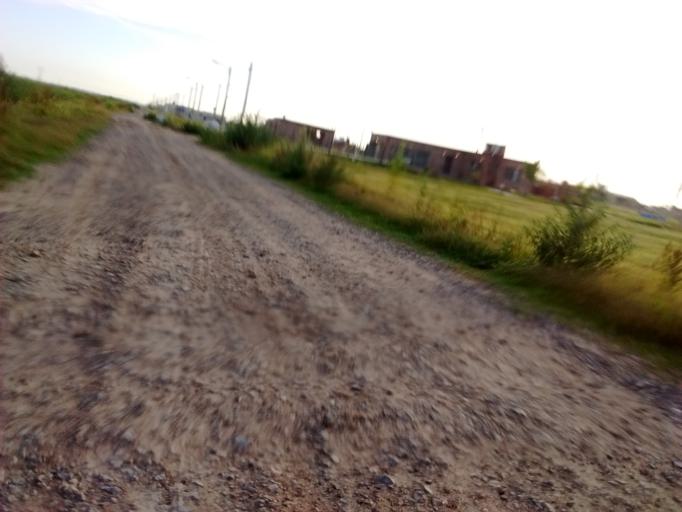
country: AR
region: Santa Fe
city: Roldan
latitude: -32.9421
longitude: -60.8754
